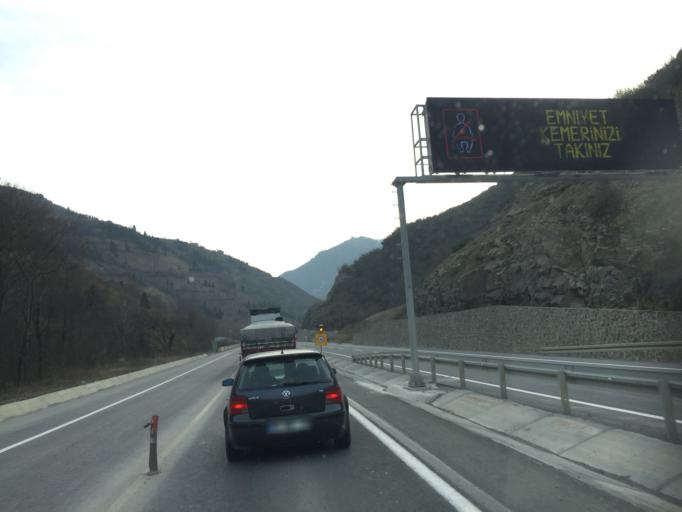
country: TR
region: Trabzon
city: Macka
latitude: 40.7926
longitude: 39.5817
